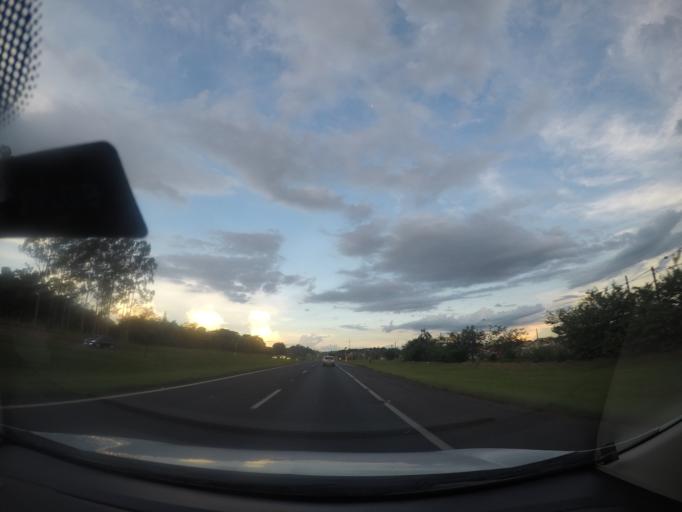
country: BR
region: Sao Paulo
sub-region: Ibate
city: Ibate
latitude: -21.9708
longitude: -47.9505
